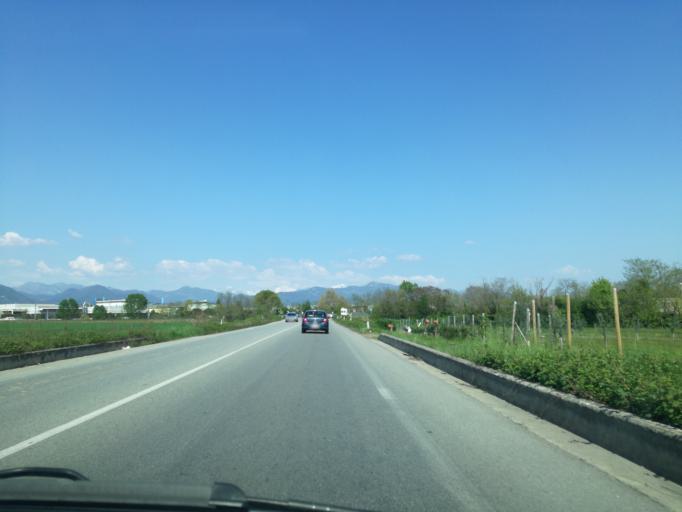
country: IT
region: Lombardy
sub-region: Provincia di Bergamo
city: Bonate Sopra
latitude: 45.6902
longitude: 9.5498
